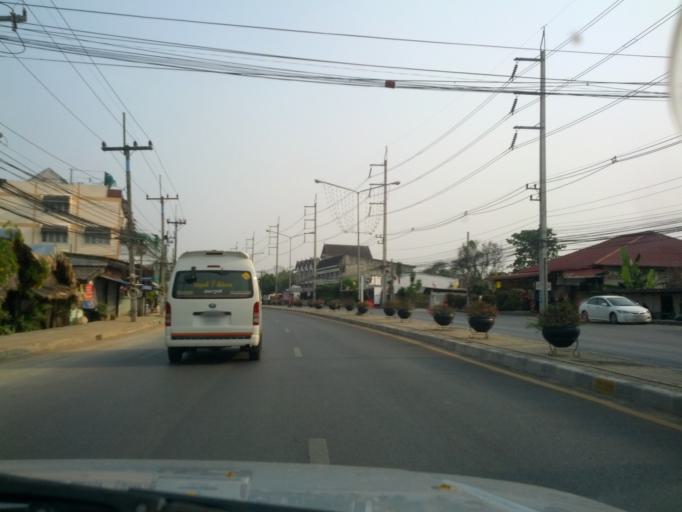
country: TH
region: Chiang Mai
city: Mae Taeng
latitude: 19.0985
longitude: 98.9358
